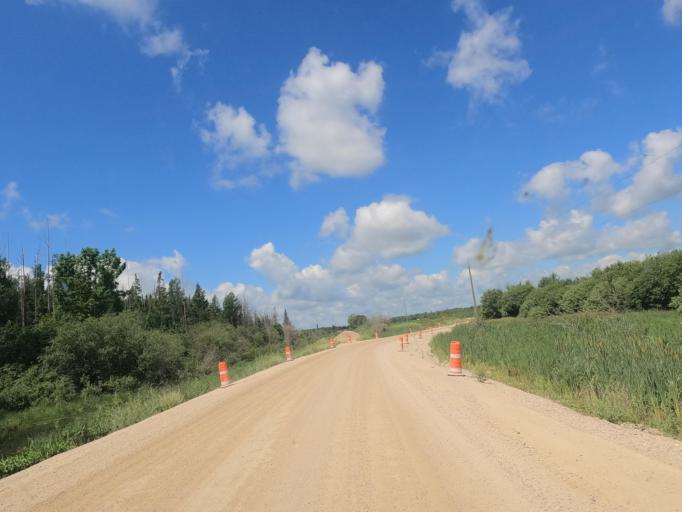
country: CA
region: Manitoba
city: Lac du Bonnet
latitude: 49.9282
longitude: -95.8650
